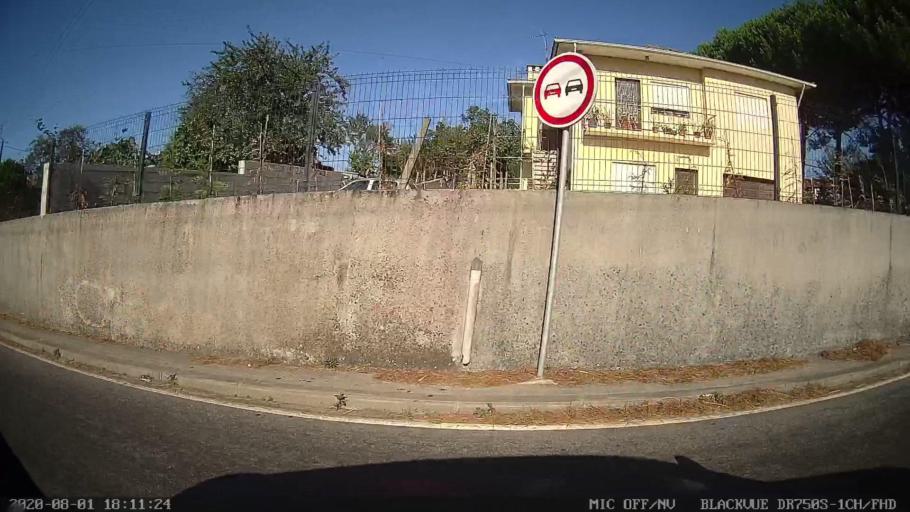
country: PT
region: Porto
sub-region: Santo Tirso
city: Sao Miguel do Couto
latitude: 41.2987
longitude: -8.4710
